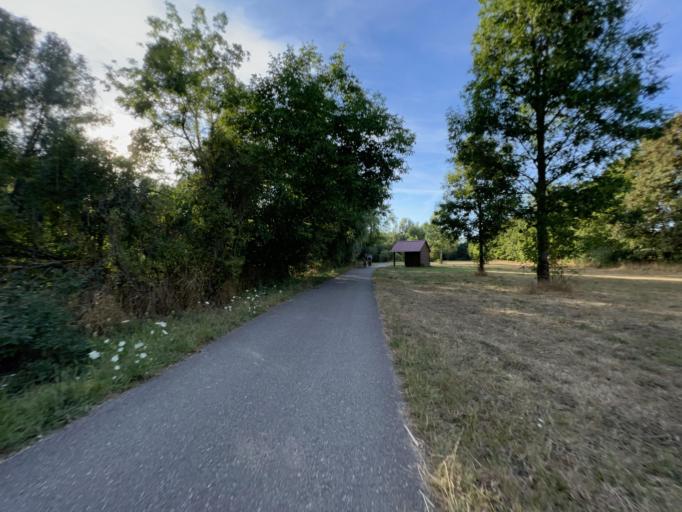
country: DE
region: North Rhine-Westphalia
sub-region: Regierungsbezirk Koln
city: Dueren
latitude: 50.8140
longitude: 6.4581
